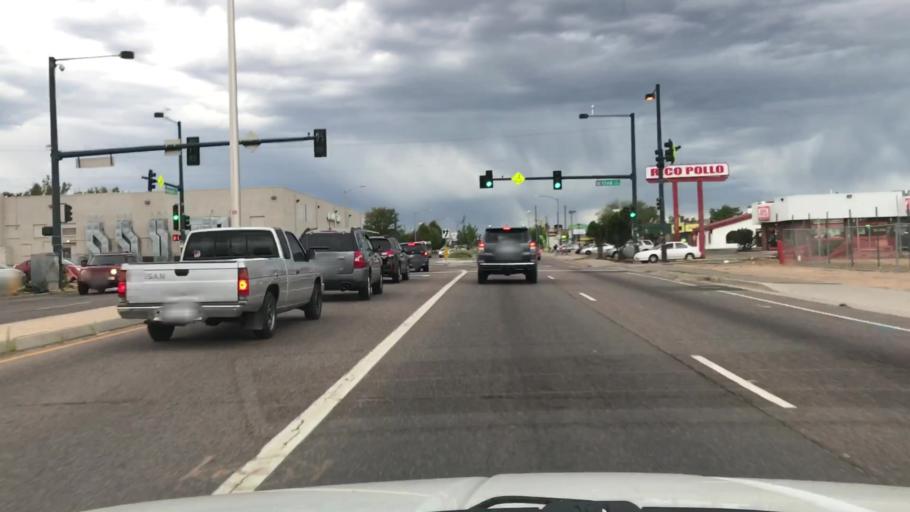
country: US
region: Colorado
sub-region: Adams County
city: Berkley
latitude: 39.7915
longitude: -105.0253
